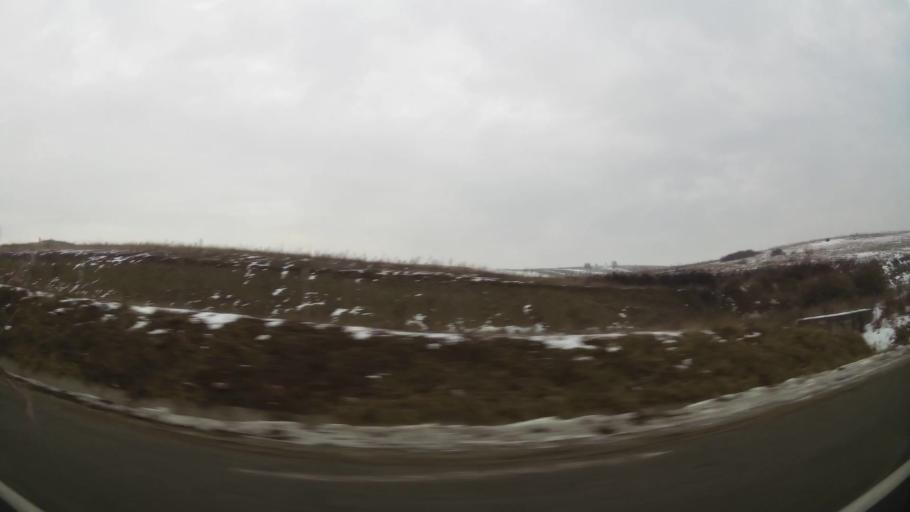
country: MK
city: Kondovo
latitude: 42.0219
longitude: 21.3308
